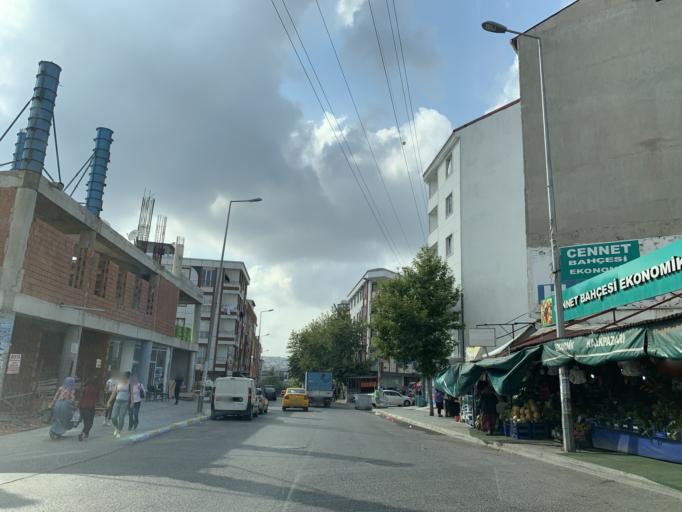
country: TR
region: Istanbul
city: Esenyurt
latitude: 41.0259
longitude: 28.6736
